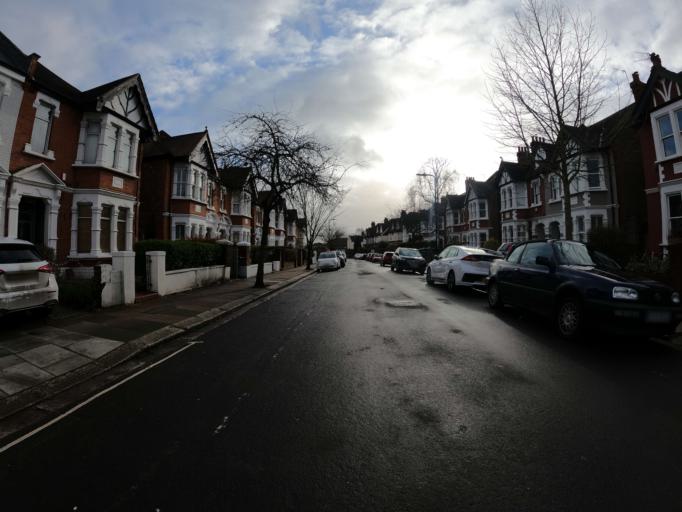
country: GB
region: England
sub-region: Greater London
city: Acton
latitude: 51.5119
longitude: -0.2636
